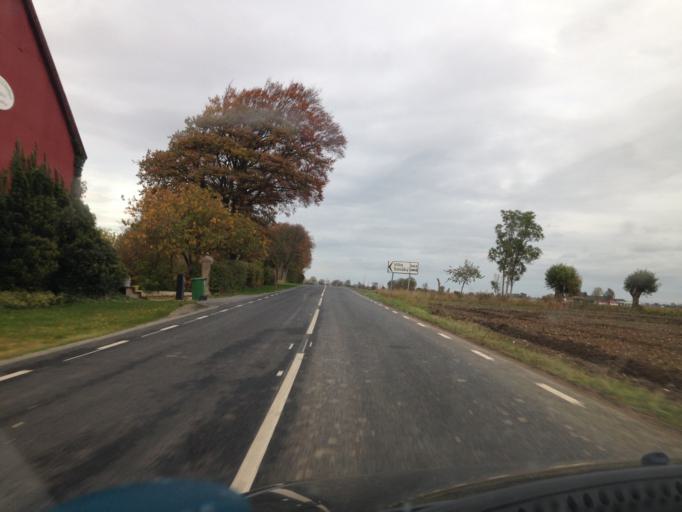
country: SE
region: Skane
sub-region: Simrishamns Kommun
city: Simrishamn
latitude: 55.4312
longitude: 14.1717
